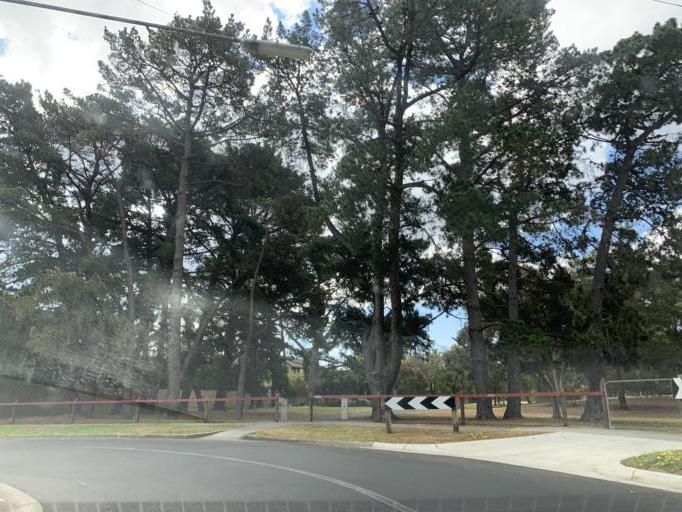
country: AU
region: Victoria
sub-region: Bayside
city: Hampton
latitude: -37.9419
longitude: 145.0161
